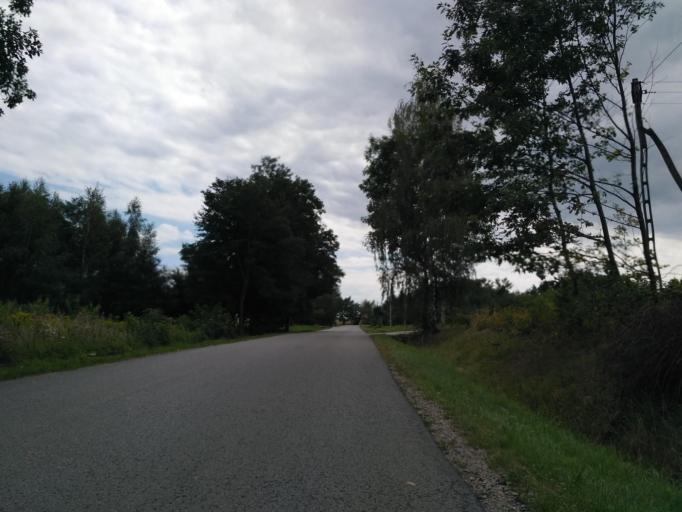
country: PL
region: Subcarpathian Voivodeship
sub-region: Powiat rzeszowski
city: Straszydle
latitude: 49.8854
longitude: 21.9920
